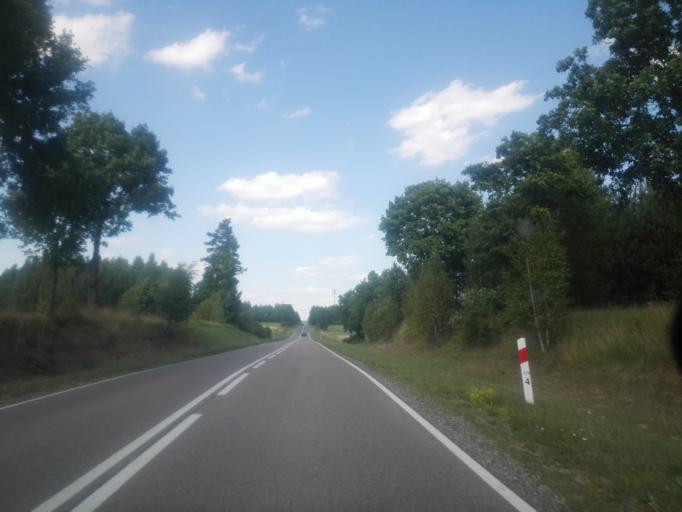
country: PL
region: Podlasie
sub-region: Powiat sejnenski
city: Sejny
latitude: 54.0248
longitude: 23.3444
